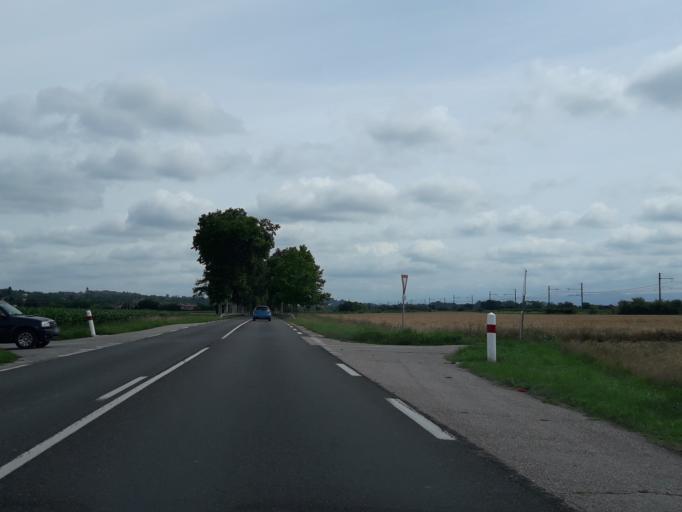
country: FR
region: Rhone-Alpes
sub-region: Departement de l'Ain
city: Perouges
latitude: 45.8768
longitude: 5.1609
